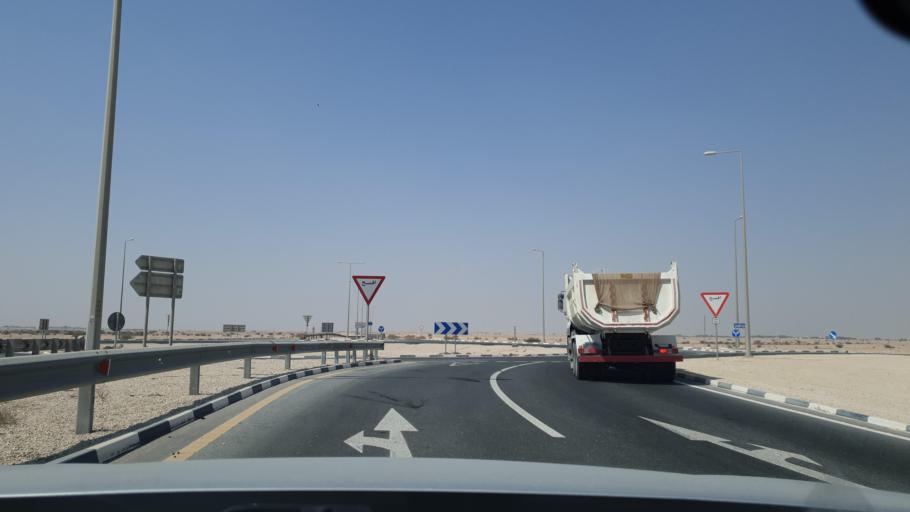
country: QA
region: Baladiyat az Za`ayin
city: Az Za`ayin
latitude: 25.6236
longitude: 51.3427
